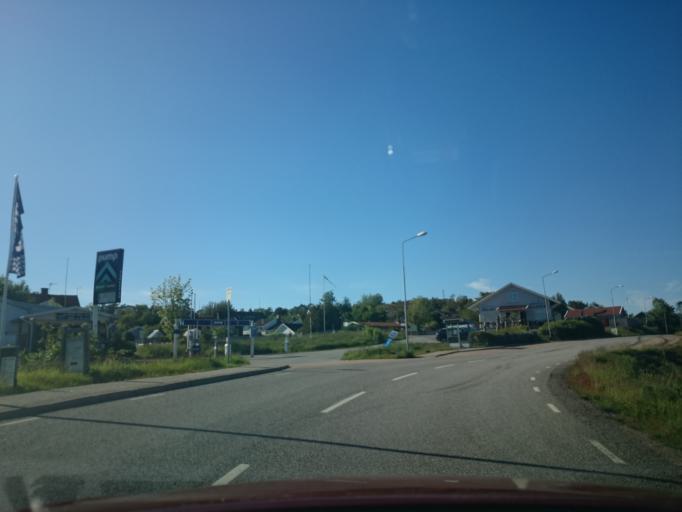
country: SE
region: Vaestra Goetaland
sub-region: Lysekils Kommun
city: Lysekil
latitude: 58.2386
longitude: 11.4574
